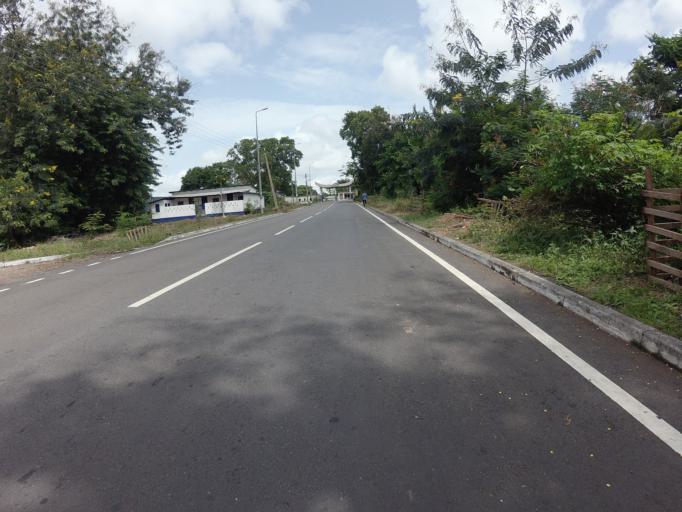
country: GH
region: Volta
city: Ho
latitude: 6.6056
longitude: 0.4590
